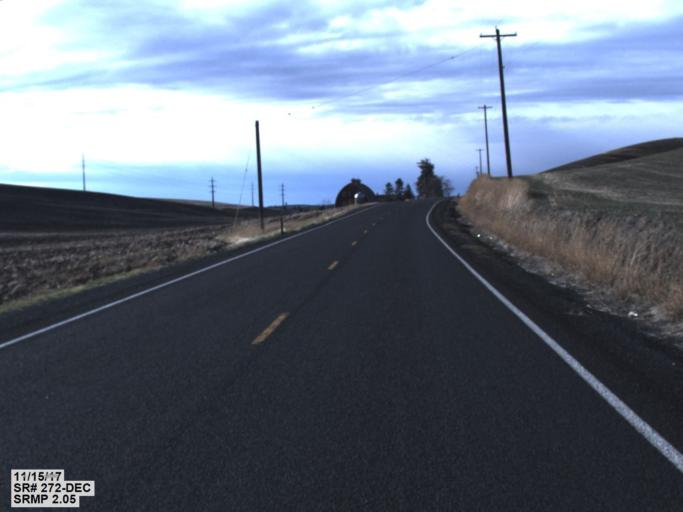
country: US
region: Washington
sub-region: Whitman County
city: Colfax
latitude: 46.8919
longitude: -117.3282
